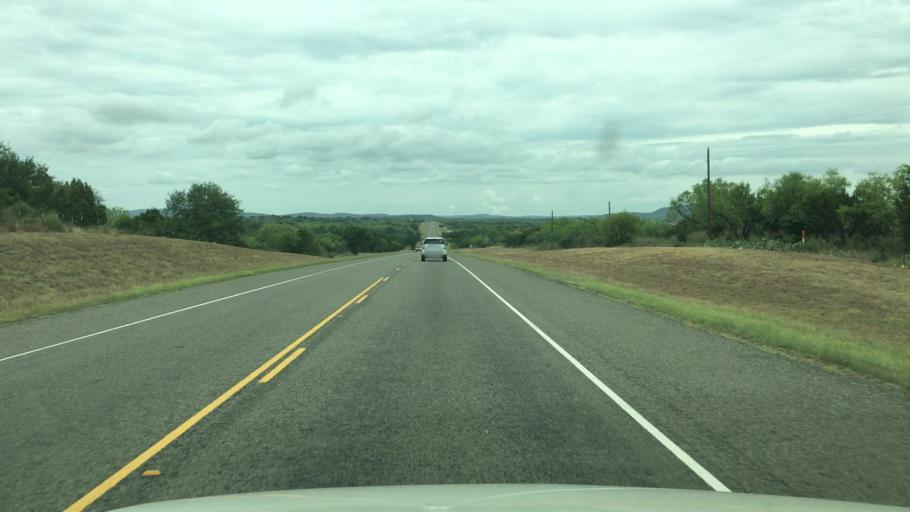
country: US
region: Texas
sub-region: Burnet County
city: Granite Shoals
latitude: 30.5515
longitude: -98.4652
